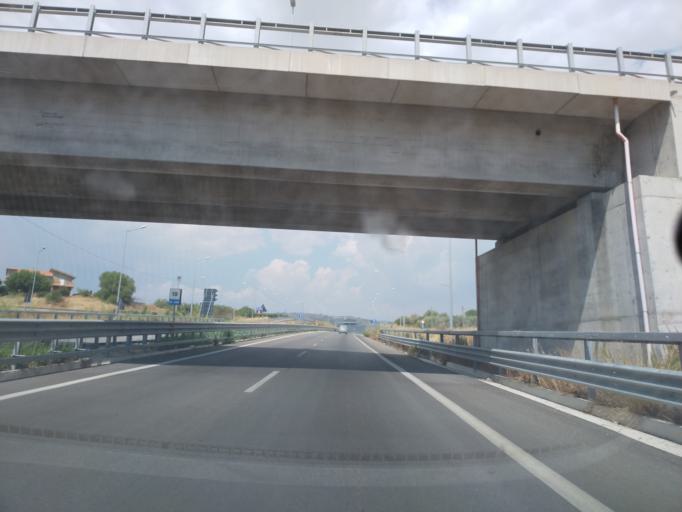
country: IT
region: Sicily
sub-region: Agrigento
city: Favara
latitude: 37.3537
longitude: 13.6803
